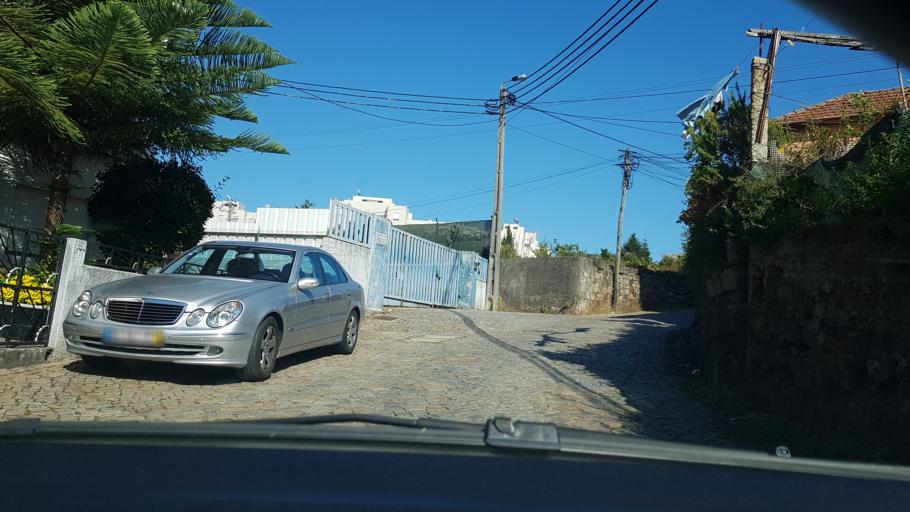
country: PT
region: Porto
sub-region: Gondomar
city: Baguim do Monte
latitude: 41.1920
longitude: -8.5435
